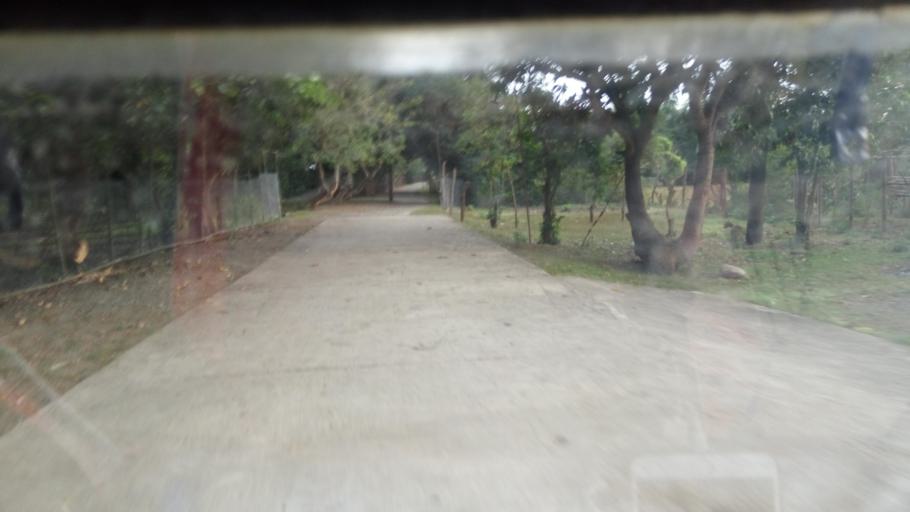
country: PH
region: Ilocos
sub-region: Province of La Union
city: Damortis
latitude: 16.2484
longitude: 120.4035
